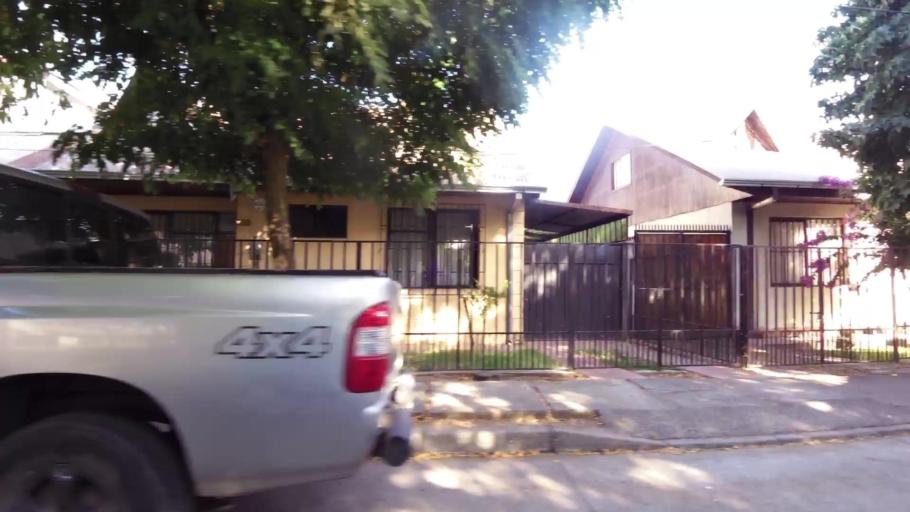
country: CL
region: Maule
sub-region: Provincia de Talca
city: Talca
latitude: -35.4109
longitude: -71.6644
